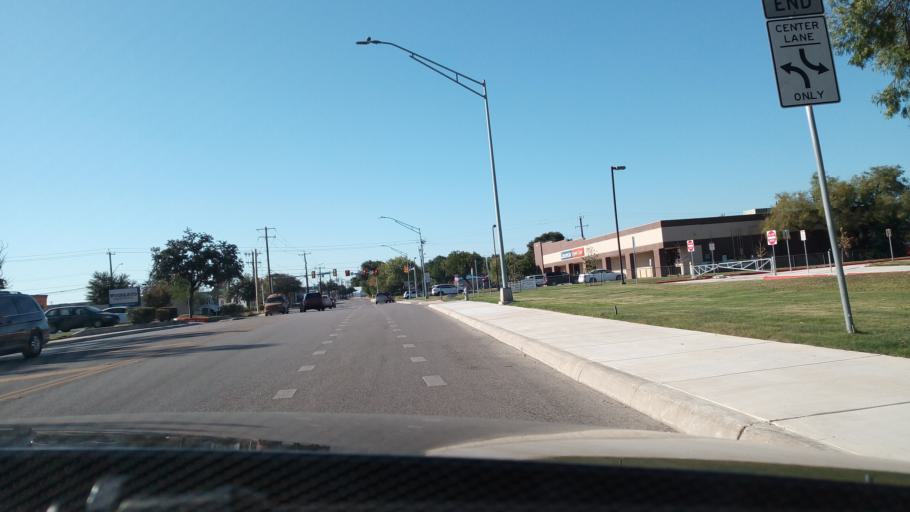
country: US
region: Texas
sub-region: Bexar County
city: Alamo Heights
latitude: 29.5320
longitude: -98.4472
